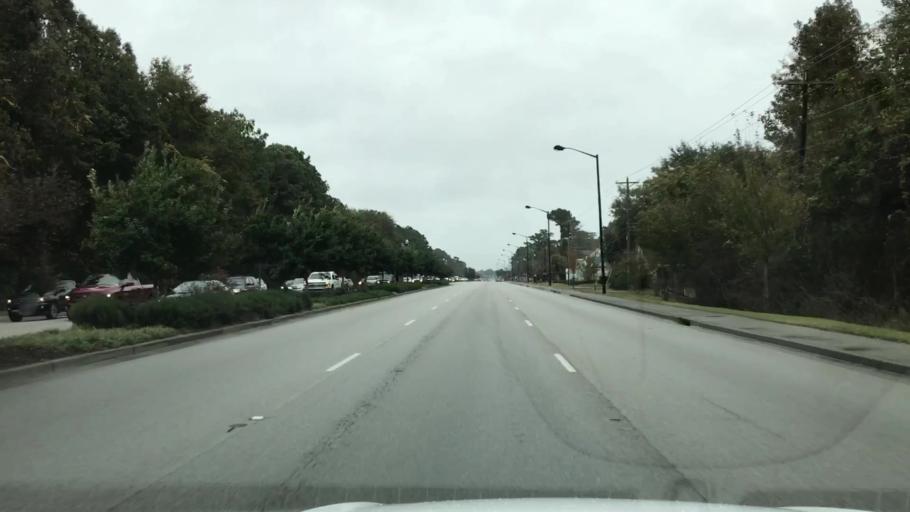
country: US
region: South Carolina
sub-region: Charleston County
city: Isle of Palms
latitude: 32.8494
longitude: -79.8079
